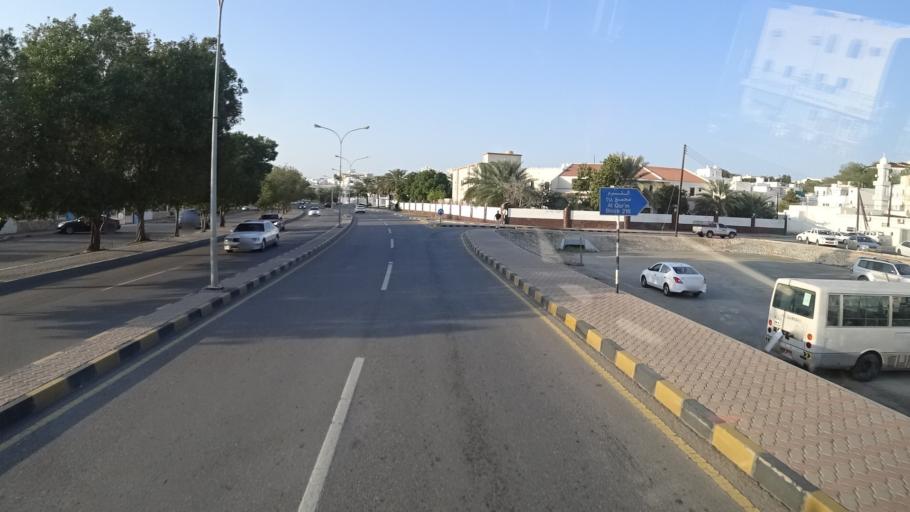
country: OM
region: Muhafazat Masqat
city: Muscat
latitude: 23.6194
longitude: 58.4948
